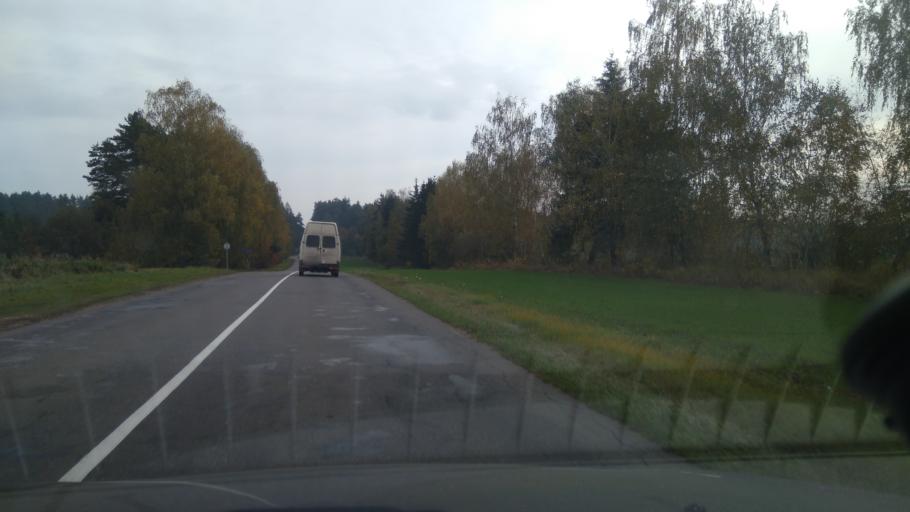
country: BY
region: Minsk
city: Rudzyensk
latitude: 53.6144
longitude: 27.7657
